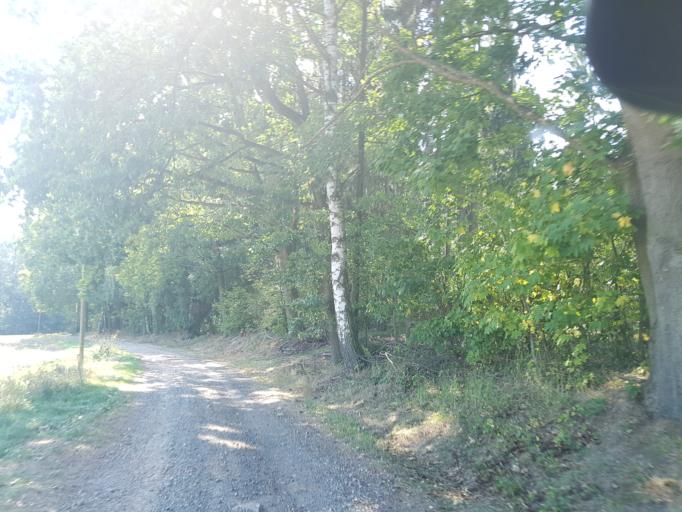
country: DE
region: Saxony
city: Kriebstein
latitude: 51.0452
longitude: 13.0070
